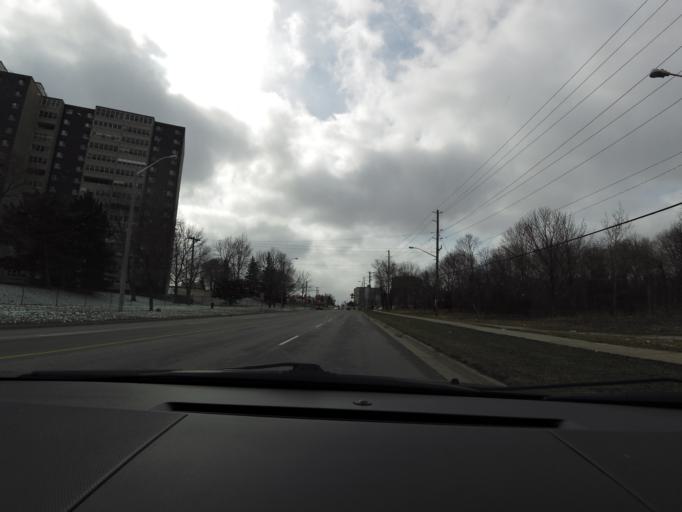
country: CA
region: Ontario
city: Waterloo
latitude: 43.4848
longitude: -80.5050
